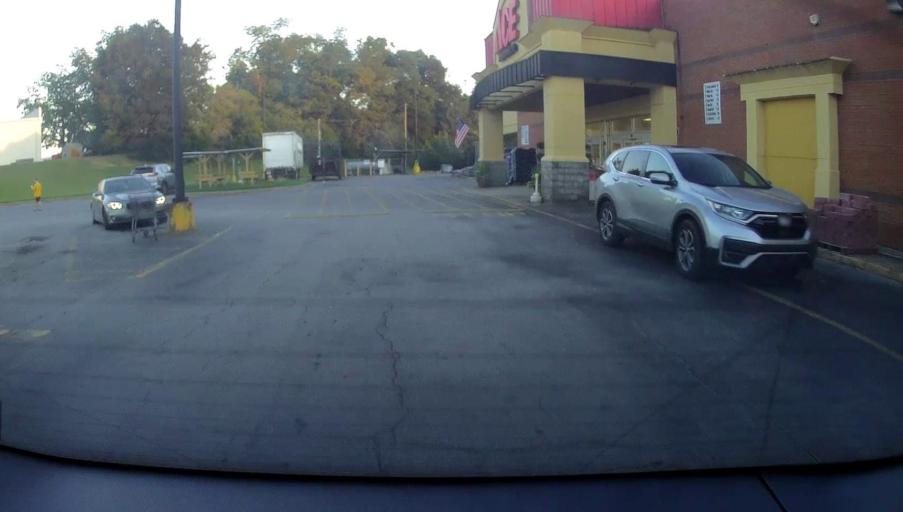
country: US
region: Georgia
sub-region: Houston County
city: Perry
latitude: 32.4656
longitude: -83.7397
